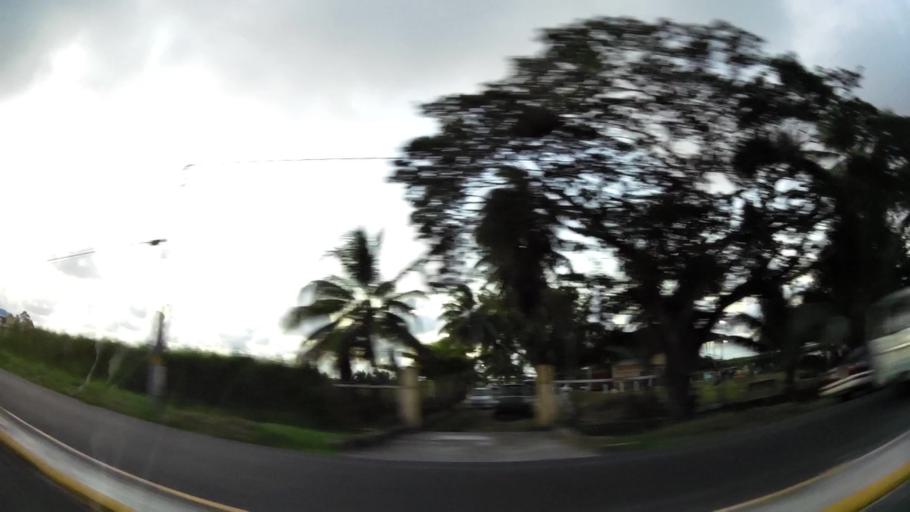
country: GY
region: Demerara-Mahaica
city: Georgetown
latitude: 6.8234
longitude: -58.1517
